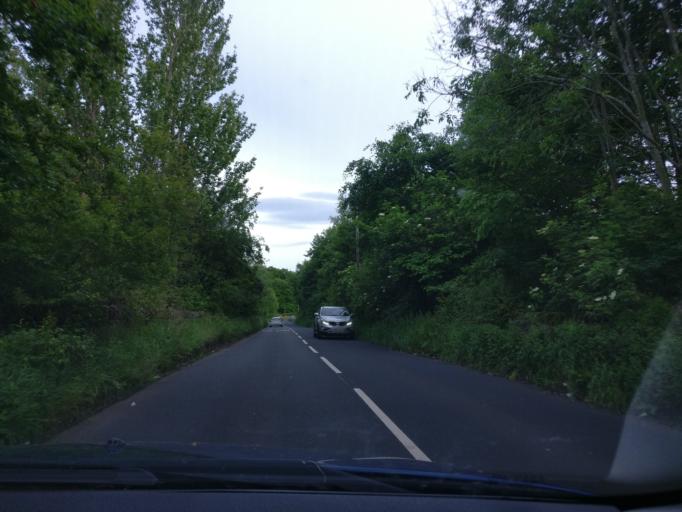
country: GB
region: Scotland
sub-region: West Lothian
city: Seafield
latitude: 55.9292
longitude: -3.1391
